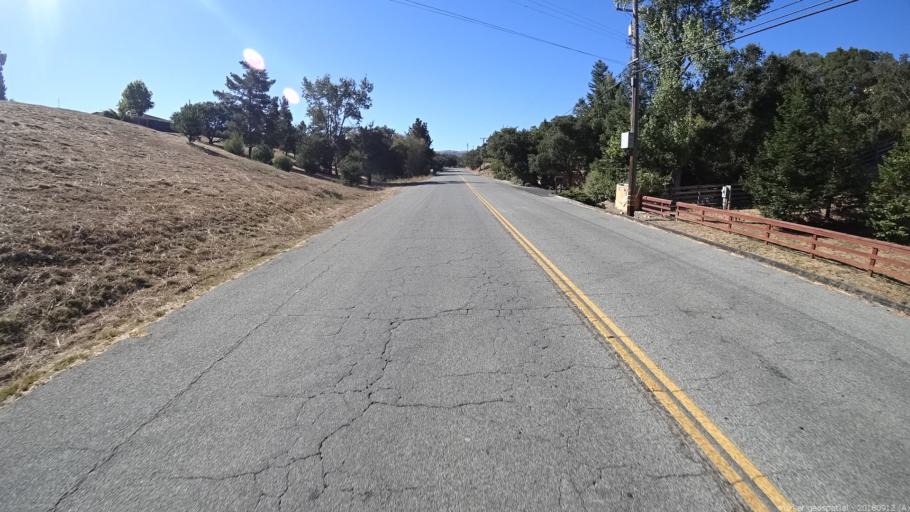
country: US
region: California
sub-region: Monterey County
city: Carmel Valley Village
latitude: 36.5708
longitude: -121.7307
